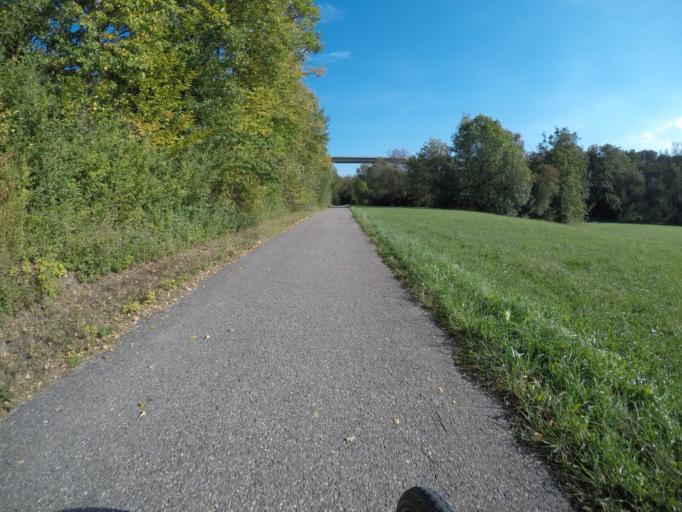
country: DE
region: Baden-Wuerttemberg
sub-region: Regierungsbezirk Stuttgart
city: Schlaitdorf
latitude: 48.6219
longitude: 9.2216
